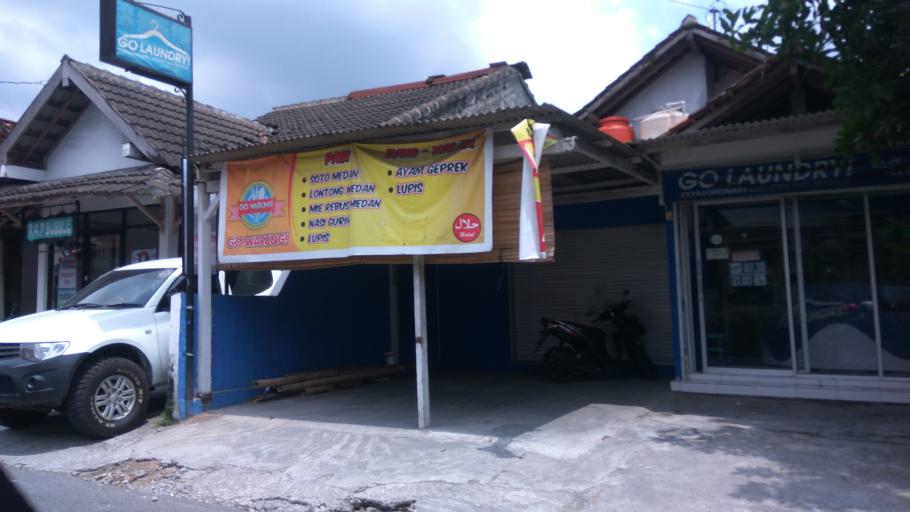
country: ID
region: Daerah Istimewa Yogyakarta
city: Depok
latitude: -7.7511
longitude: 110.4109
